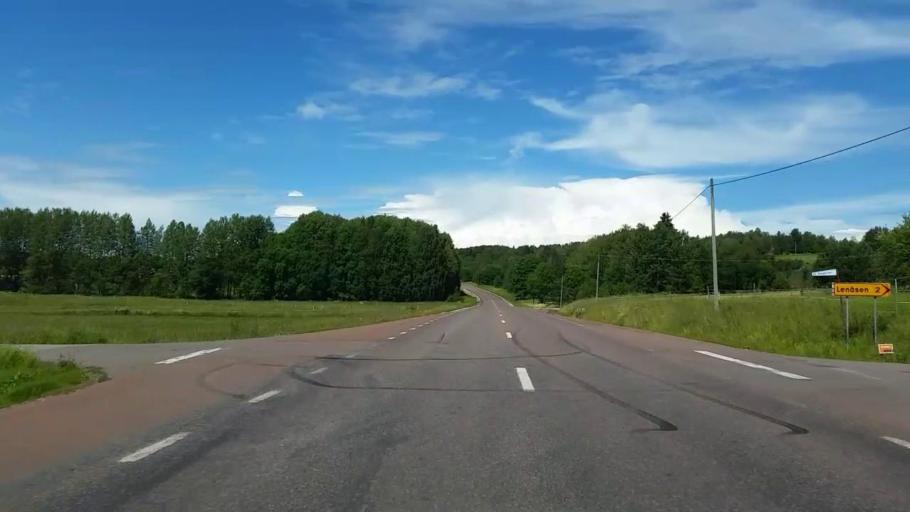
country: SE
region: Dalarna
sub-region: Rattviks Kommun
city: Raettvik
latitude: 61.0106
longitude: 15.2174
